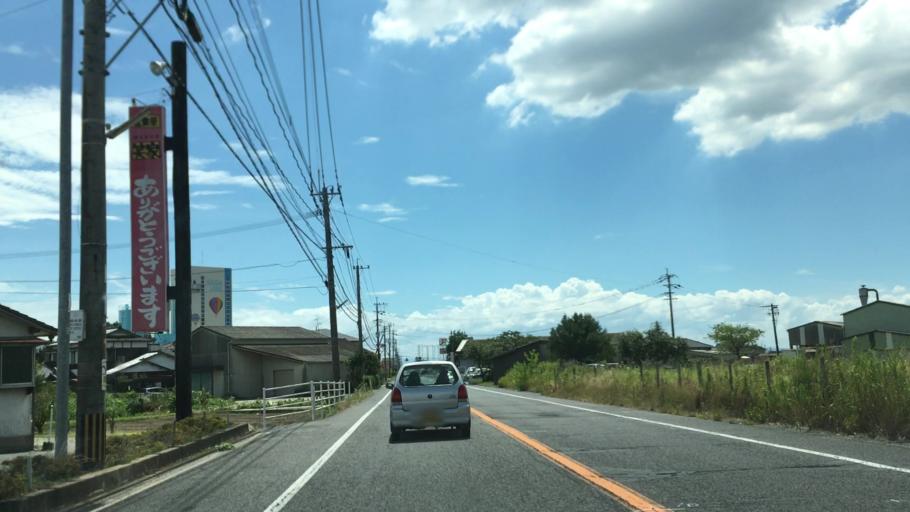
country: JP
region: Saga Prefecture
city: Kanzakimachi-kanzaki
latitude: 33.2836
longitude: 130.3464
